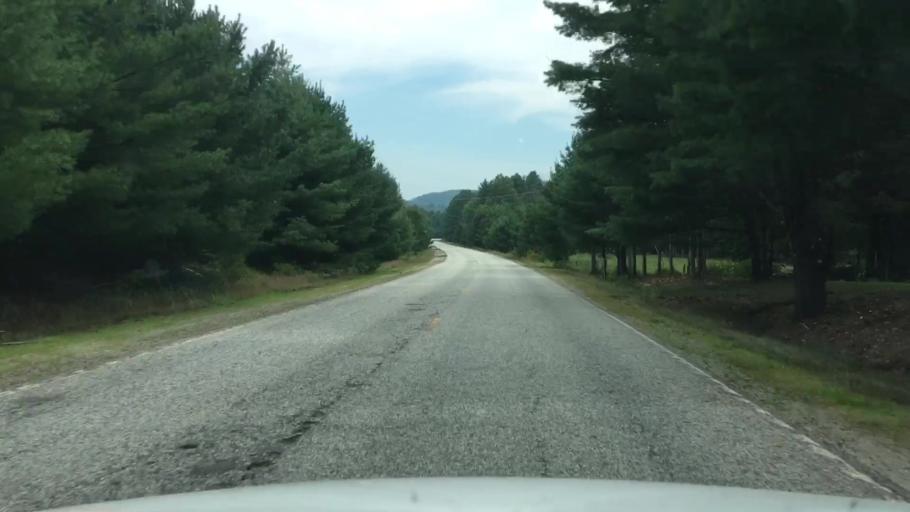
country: US
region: Maine
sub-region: Oxford County
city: Rumford
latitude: 44.5903
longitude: -70.7366
